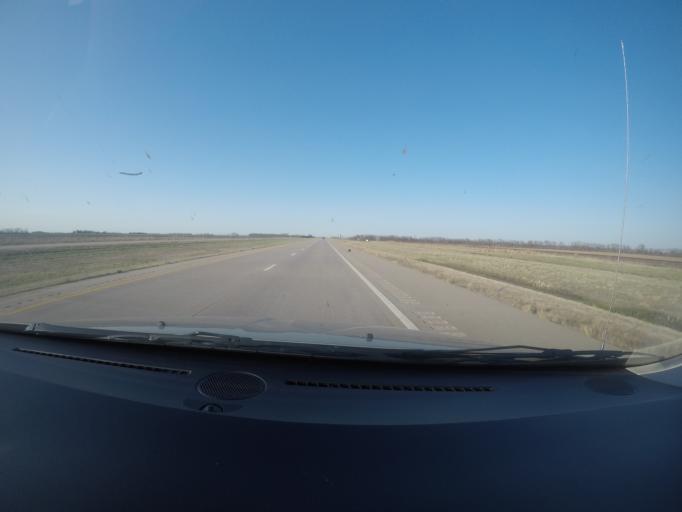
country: US
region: Kansas
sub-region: McPherson County
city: Inman
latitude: 38.2626
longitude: -97.7547
